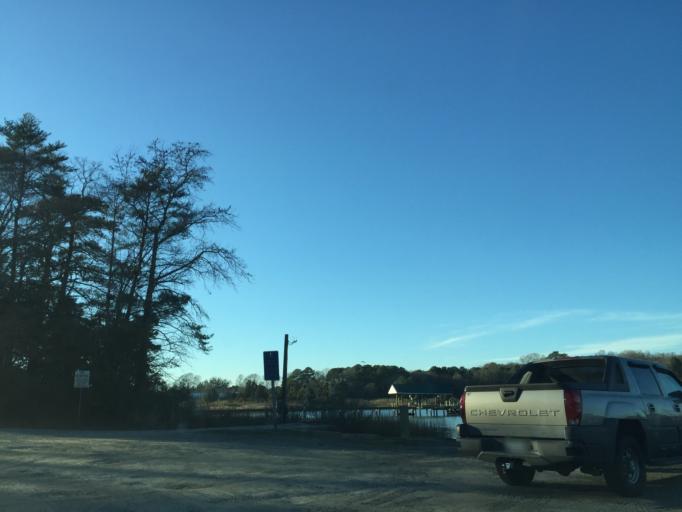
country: US
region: Virginia
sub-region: Isle of Wight County
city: Carrollton
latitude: 37.0801
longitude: -76.5229
